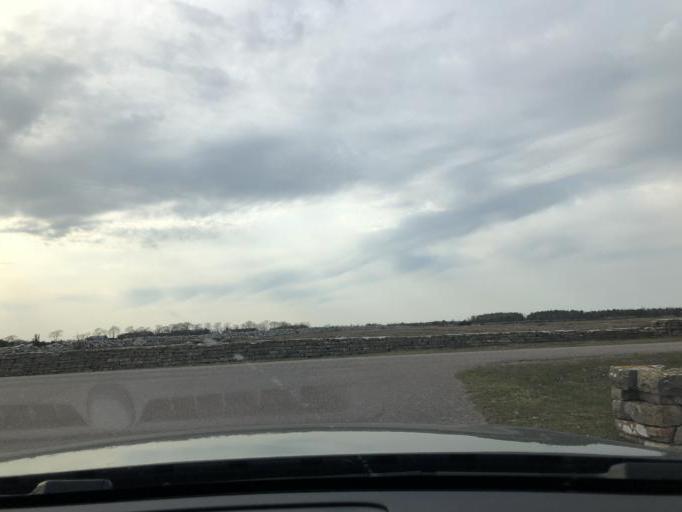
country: SE
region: Kalmar
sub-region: Morbylanga Kommun
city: Moerbylanga
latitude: 56.2926
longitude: 16.4838
